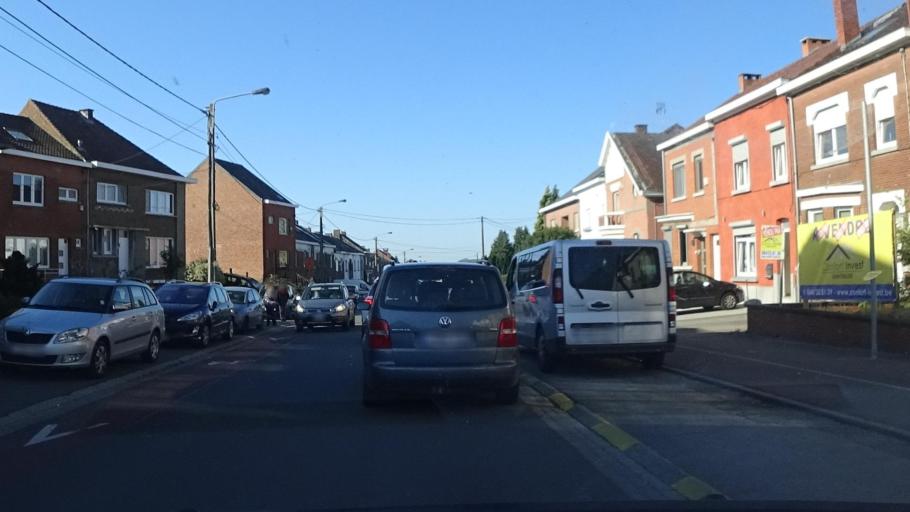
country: BE
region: Wallonia
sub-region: Province du Hainaut
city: La Louviere
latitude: 50.4647
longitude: 4.1790
